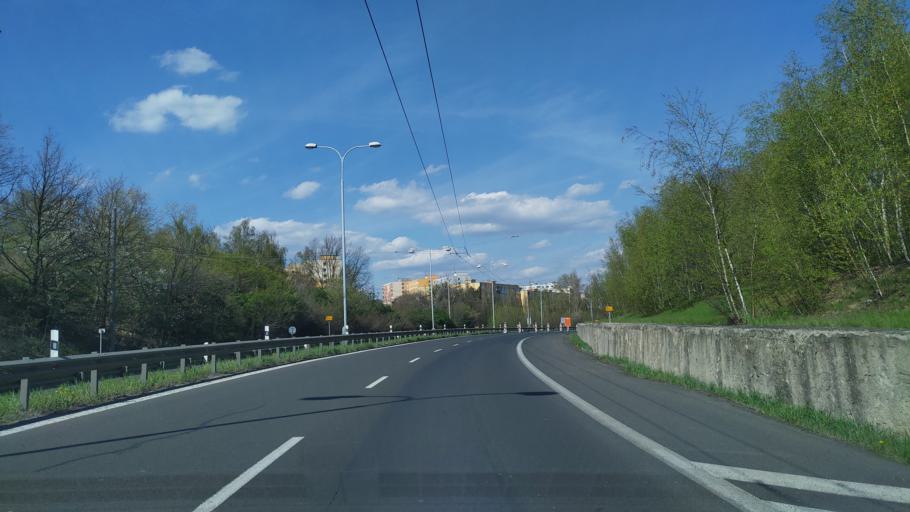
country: CZ
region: Ustecky
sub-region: Okres Chomutov
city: Chomutov
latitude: 50.4748
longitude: 13.4149
